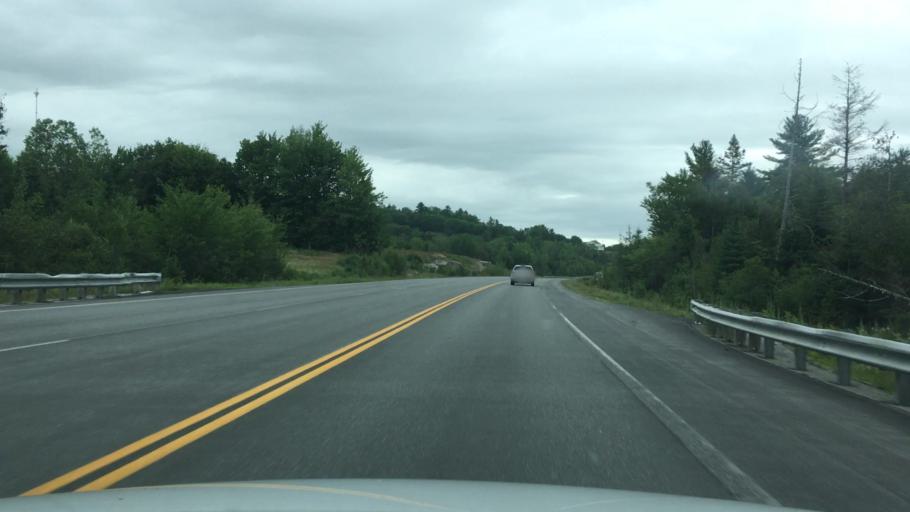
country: US
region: Maine
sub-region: Hancock County
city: Franklin
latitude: 44.8543
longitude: -68.3256
